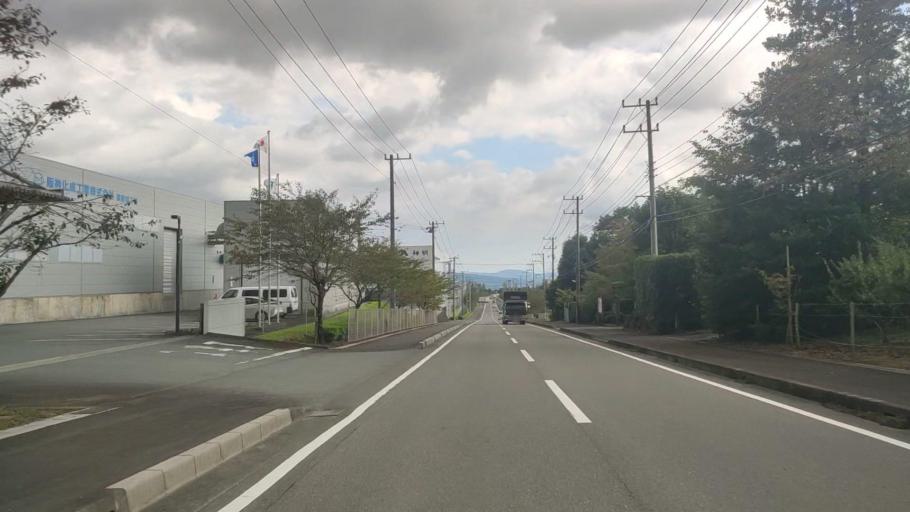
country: JP
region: Shizuoka
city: Gotemba
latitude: 35.2744
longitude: 138.8932
